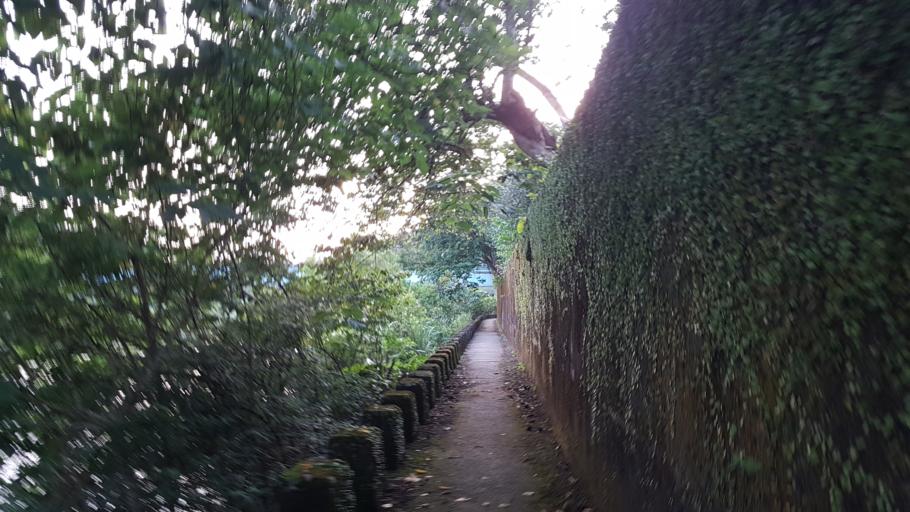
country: TW
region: Taiwan
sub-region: Yilan
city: Yilan
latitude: 24.9347
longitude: 121.7004
